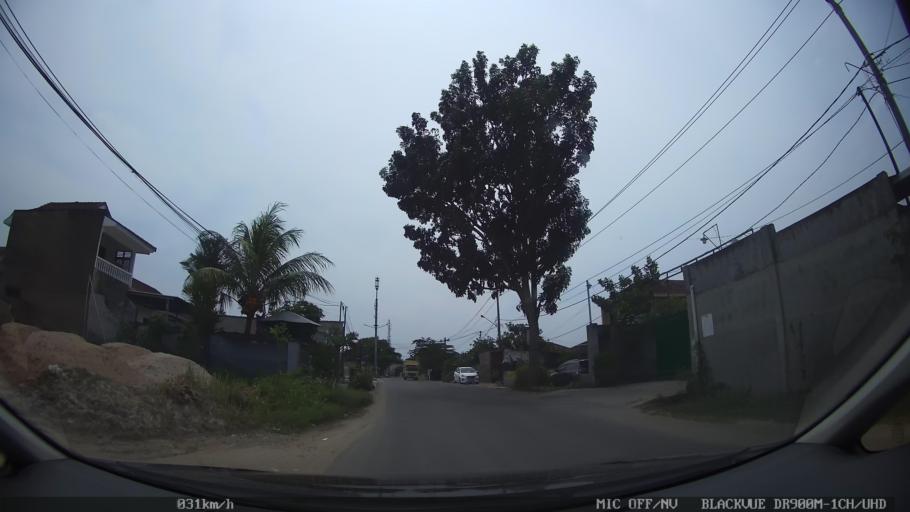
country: ID
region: Lampung
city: Bandarlampung
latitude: -5.4191
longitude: 105.2861
